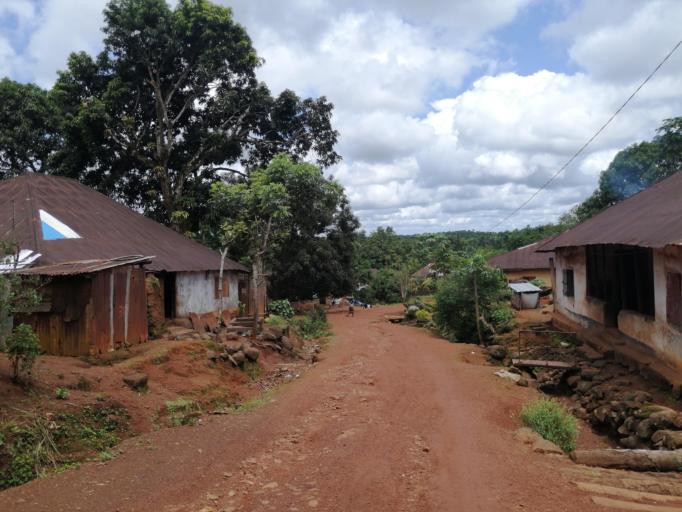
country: SL
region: Northern Province
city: Port Loko
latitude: 8.7662
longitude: -12.7923
